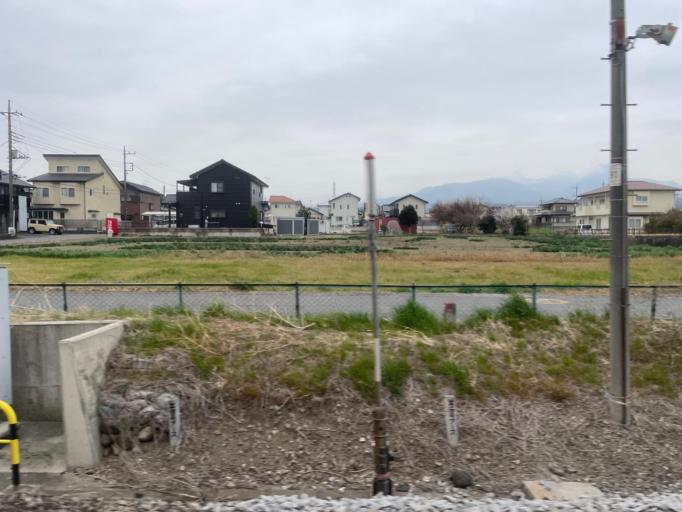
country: JP
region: Gunma
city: Shibukawa
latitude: 36.4557
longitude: 139.0207
